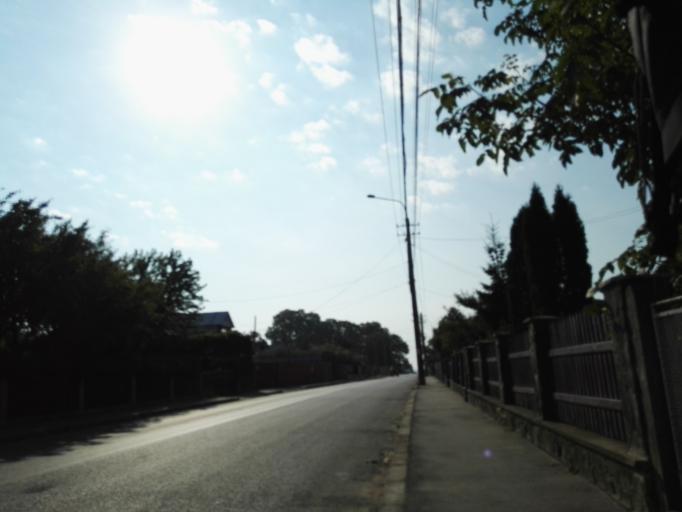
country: RO
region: Suceava
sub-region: Municipiul Falticeni
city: Falticeni
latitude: 47.4666
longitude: 26.2843
